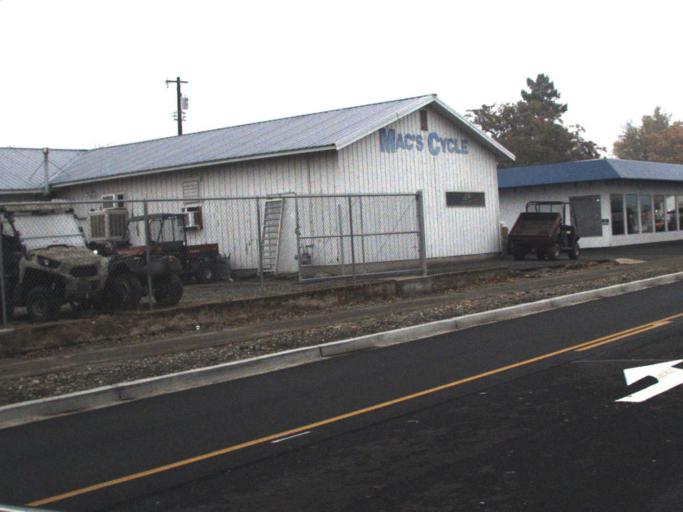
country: US
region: Washington
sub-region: Asotin County
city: Clarkston
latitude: 46.4199
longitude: -117.0477
